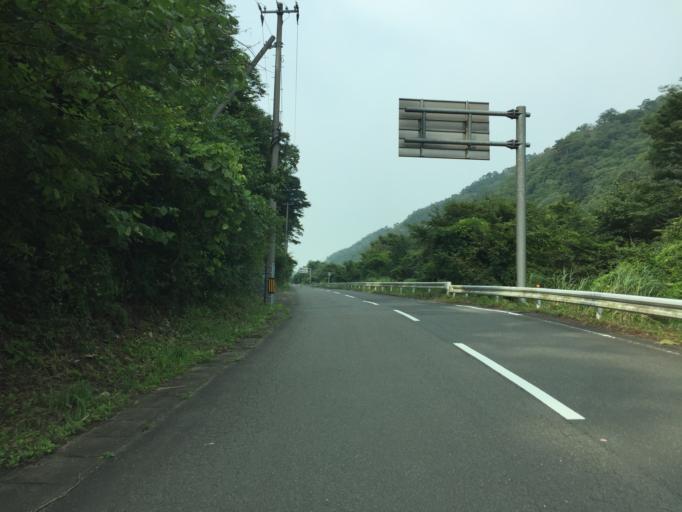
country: JP
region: Fukushima
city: Namie
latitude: 37.5783
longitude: 140.8834
